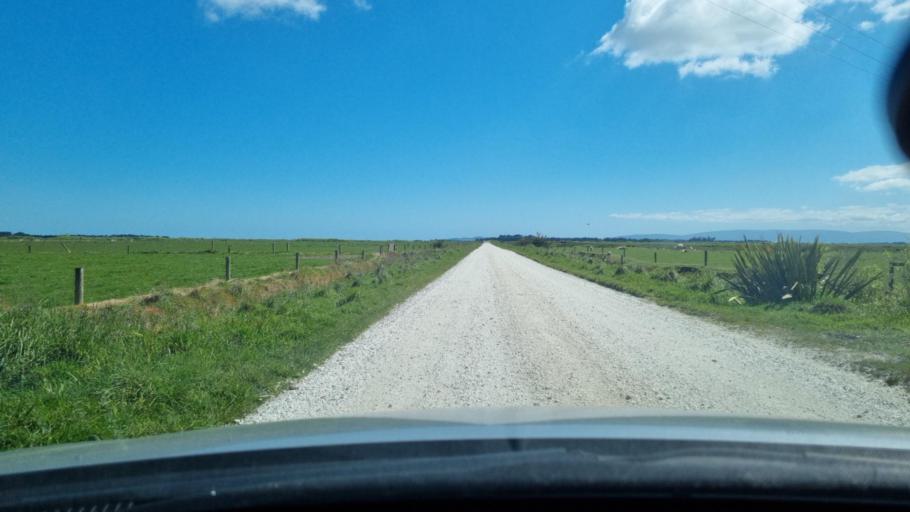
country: NZ
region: Southland
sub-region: Invercargill City
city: Invercargill
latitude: -46.3693
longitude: 168.2604
